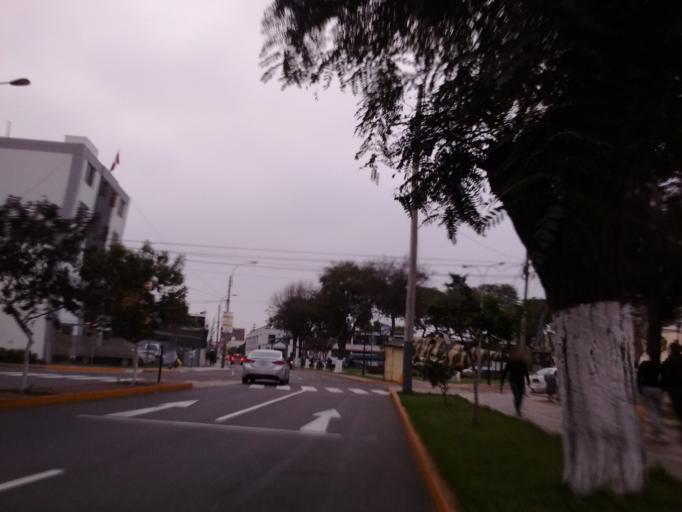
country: PE
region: Lima
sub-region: Lima
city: San Isidro
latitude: -12.0788
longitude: -77.0604
